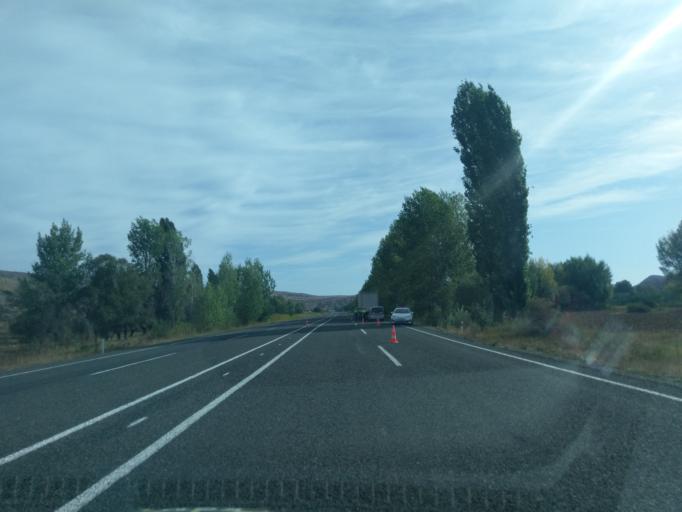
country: TR
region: Sivas
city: Zara
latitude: 39.8511
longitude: 37.8544
